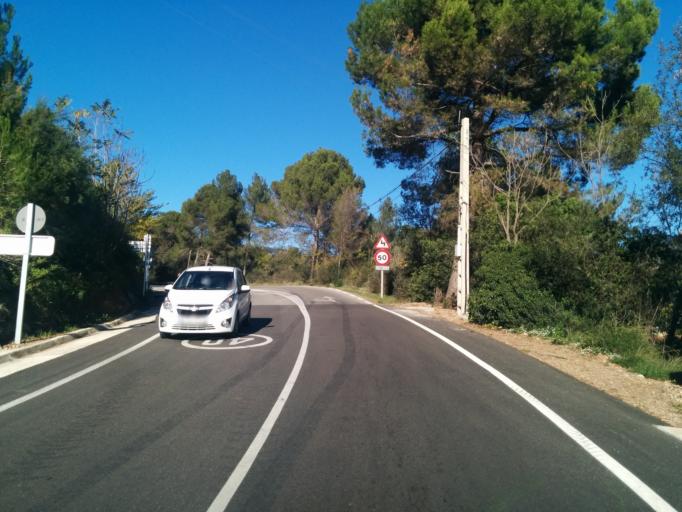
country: ES
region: Catalonia
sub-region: Provincia de Barcelona
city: Matadepera
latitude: 41.6051
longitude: 2.0159
